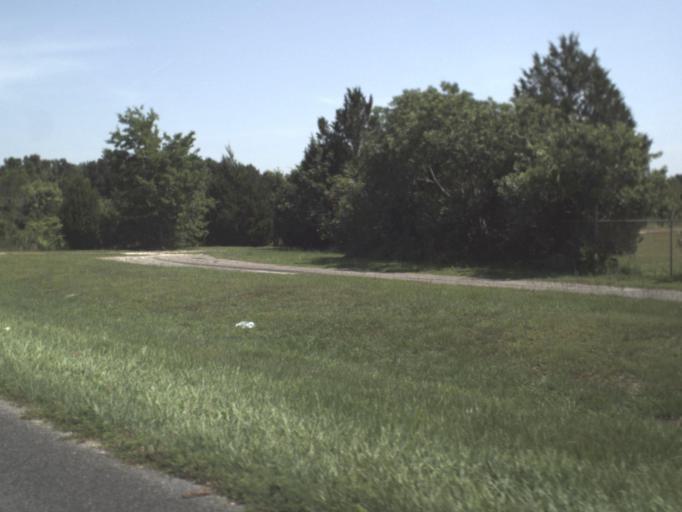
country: US
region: Florida
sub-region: Levy County
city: Manatee Road
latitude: 29.5173
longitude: -82.8796
